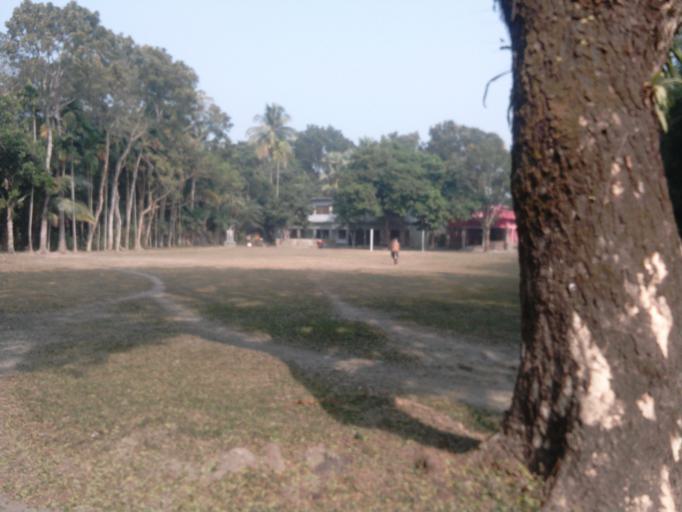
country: BD
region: Khulna
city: Kesabpur
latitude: 22.7500
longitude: 89.2462
